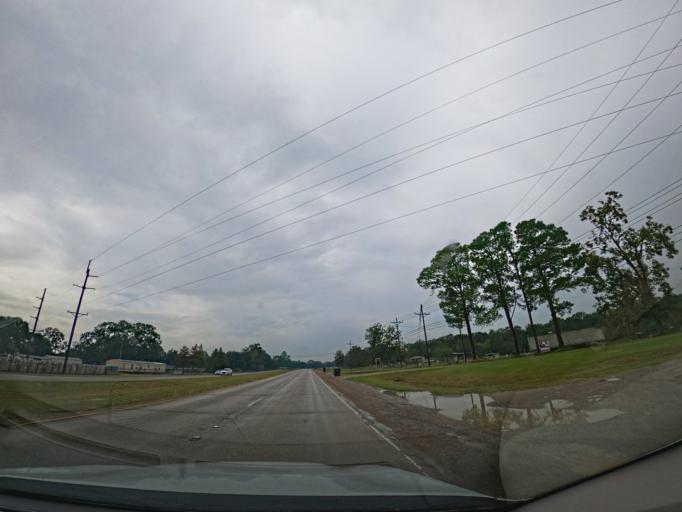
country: US
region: Louisiana
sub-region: Iberia Parish
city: Delcambre
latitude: 29.9701
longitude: -91.9059
